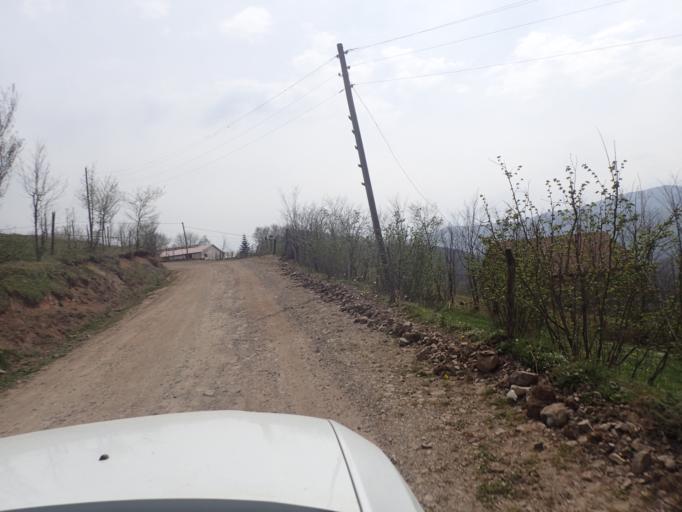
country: TR
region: Ordu
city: Aybasti
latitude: 40.7065
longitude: 37.2927
